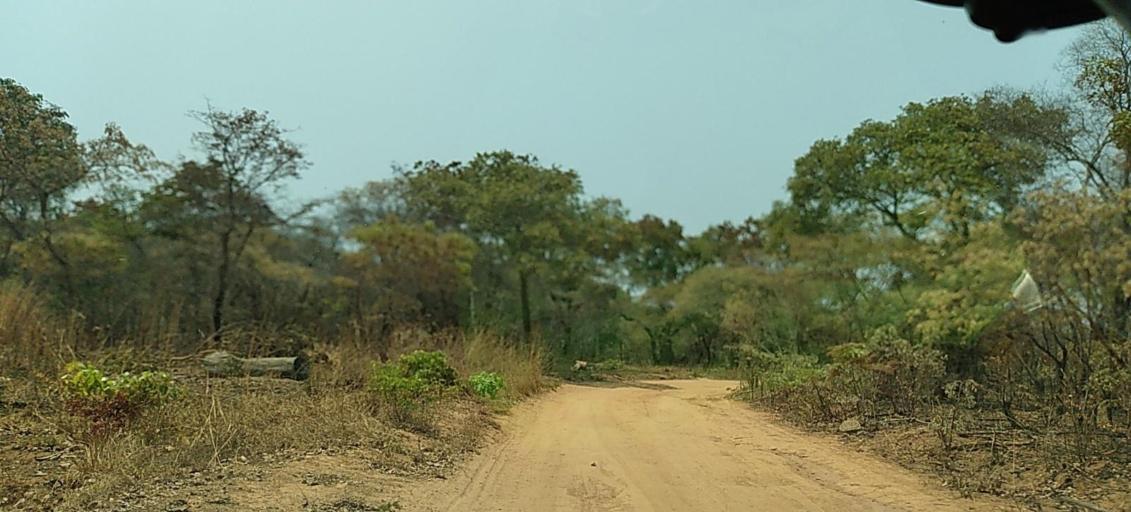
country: ZM
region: North-Western
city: Kabompo
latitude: -13.7100
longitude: 24.3269
